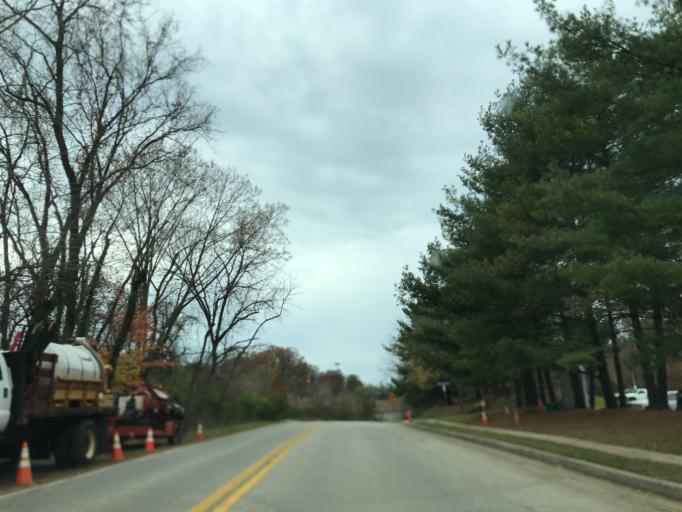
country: US
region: Maryland
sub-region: Baltimore County
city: Charlestown
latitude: 39.2645
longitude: -76.7088
